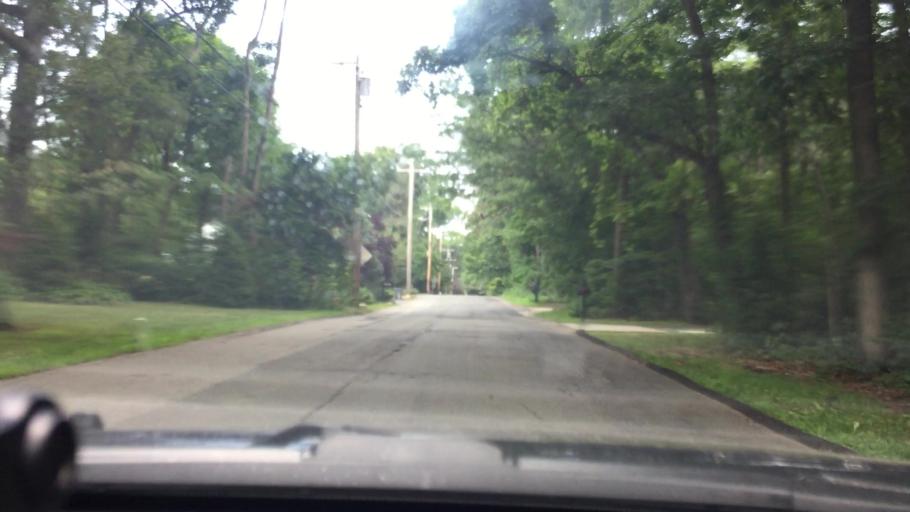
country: US
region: New York
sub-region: Suffolk County
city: Mount Sinai
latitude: 40.9249
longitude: -73.0148
